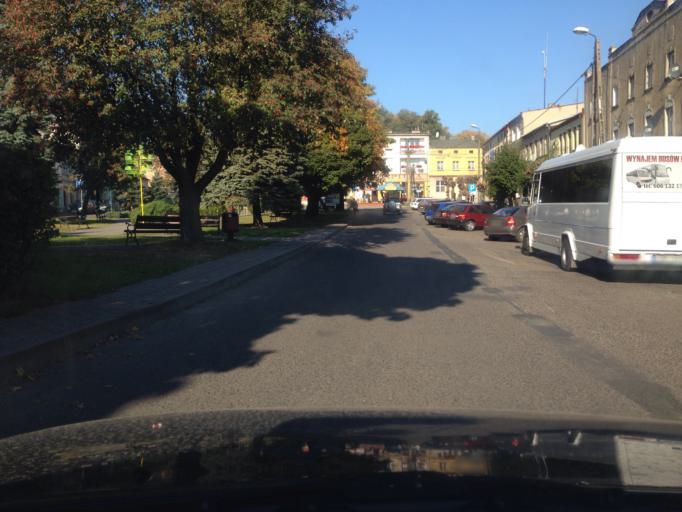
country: PL
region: Kujawsko-Pomorskie
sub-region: Powiat brodnicki
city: Gorzno
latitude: 53.1979
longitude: 19.6453
